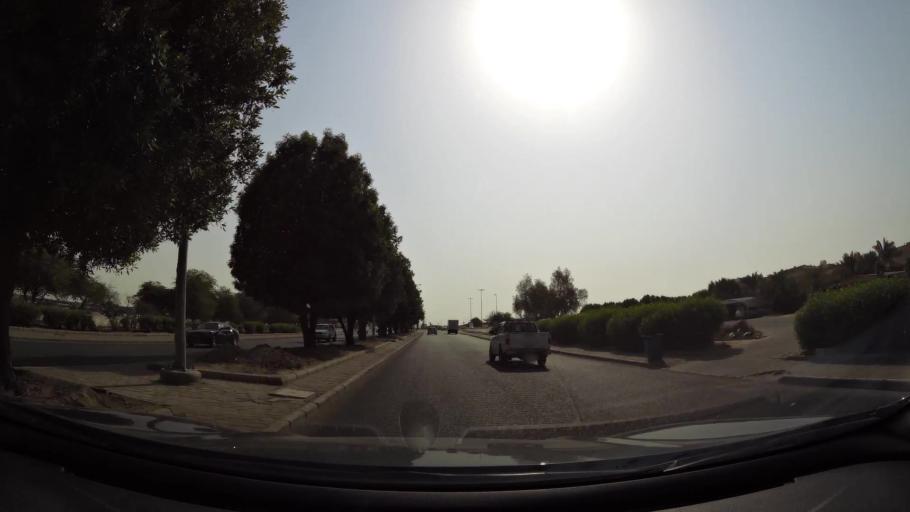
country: KW
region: Muhafazat al Jahra'
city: Al Jahra'
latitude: 29.3210
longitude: 47.6596
